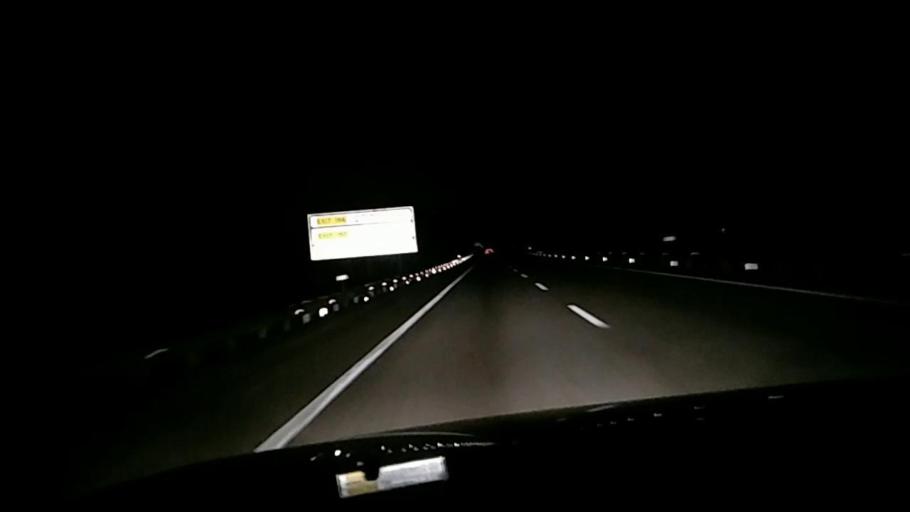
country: MY
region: Perak
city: Parit Buntar
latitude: 5.1400
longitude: 100.5129
